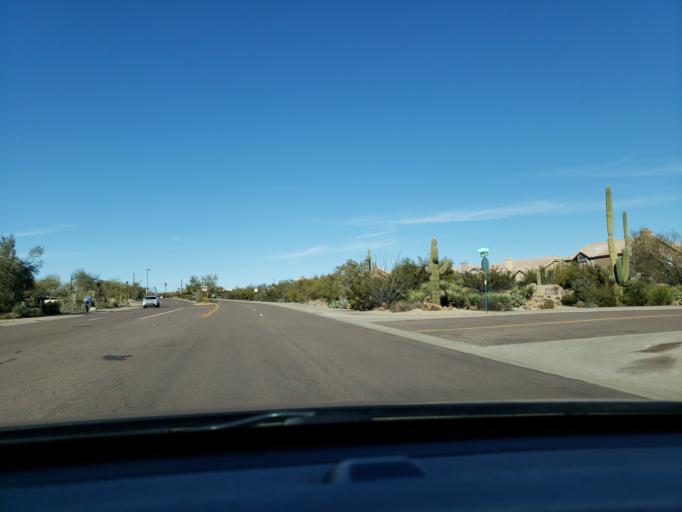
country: US
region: Arizona
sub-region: Maricopa County
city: Carefree
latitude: 33.7394
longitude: -111.8439
